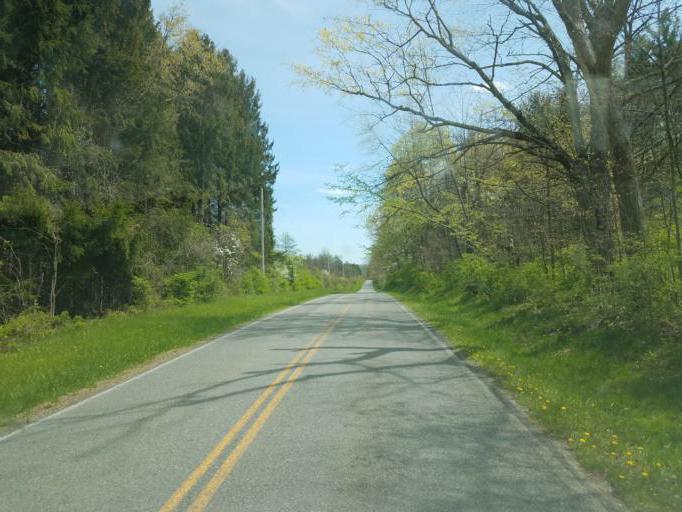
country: US
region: Ohio
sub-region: Summit County
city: Peninsula
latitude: 41.2331
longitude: -81.5652
